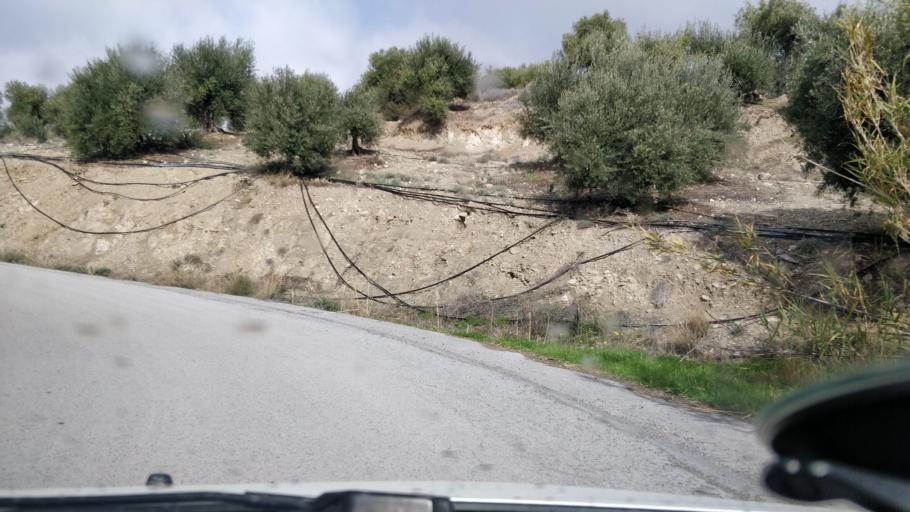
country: GR
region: Crete
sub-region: Nomos Lasithiou
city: Gra Liyia
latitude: 34.9966
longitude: 25.5132
